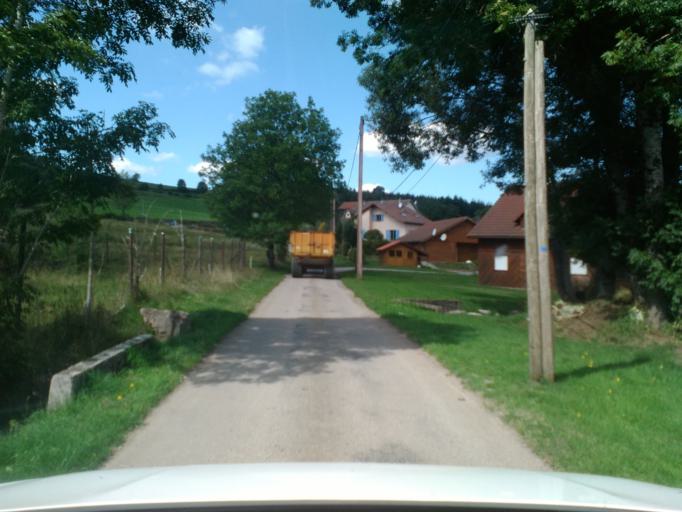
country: FR
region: Lorraine
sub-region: Departement des Vosges
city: Corcieux
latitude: 48.1482
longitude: 6.9166
